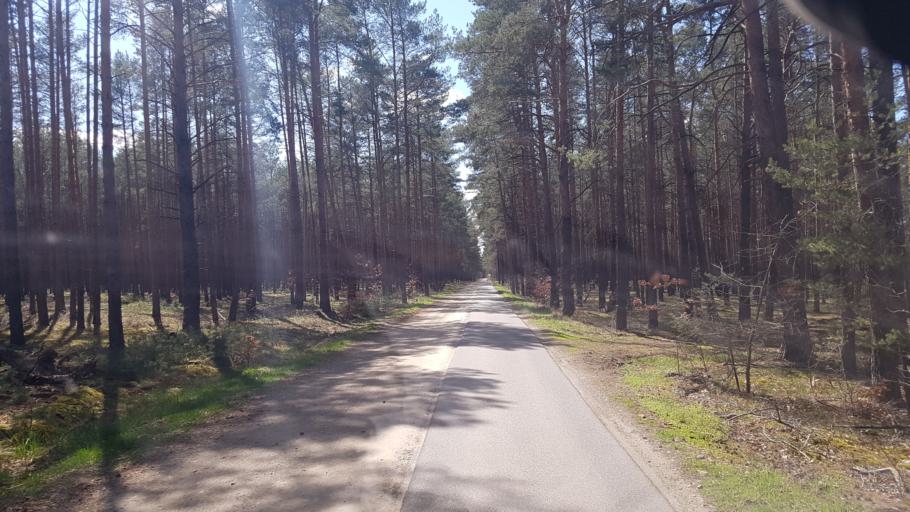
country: DE
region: Brandenburg
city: Bad Liebenwerda
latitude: 51.5258
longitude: 13.4579
